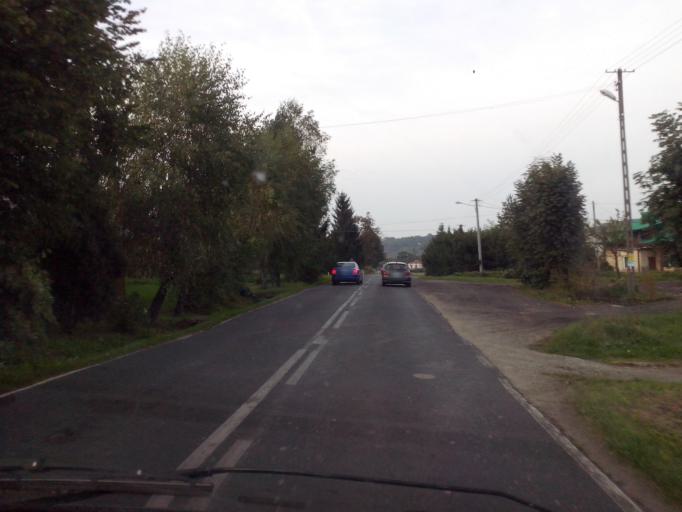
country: PL
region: Subcarpathian Voivodeship
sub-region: Powiat strzyzowski
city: Strzyzow
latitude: 49.8292
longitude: 21.8269
